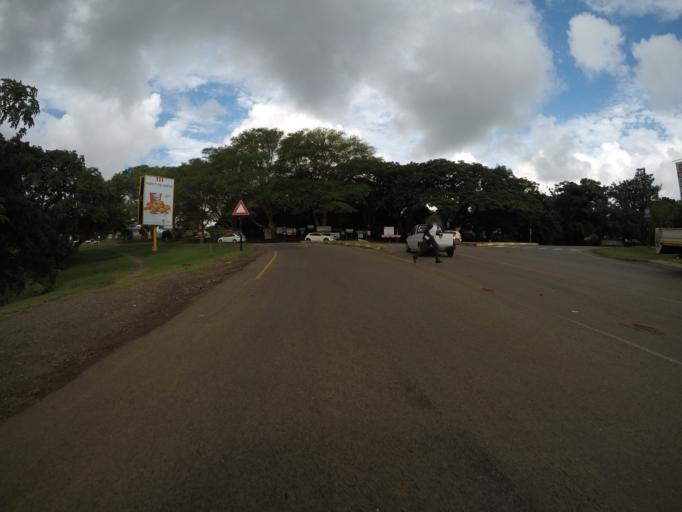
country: ZA
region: KwaZulu-Natal
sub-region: uMkhanyakude District Municipality
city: Mtubatuba
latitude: -28.4178
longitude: 32.1832
